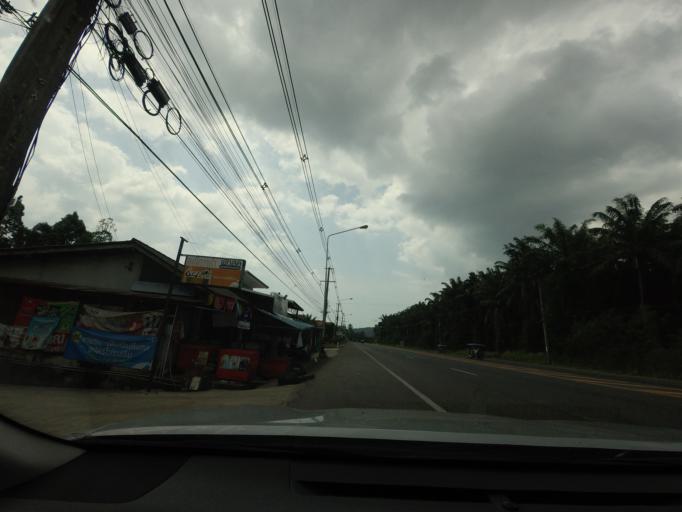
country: TH
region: Phangnga
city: Ban Ao Nang
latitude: 8.0600
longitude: 98.7833
